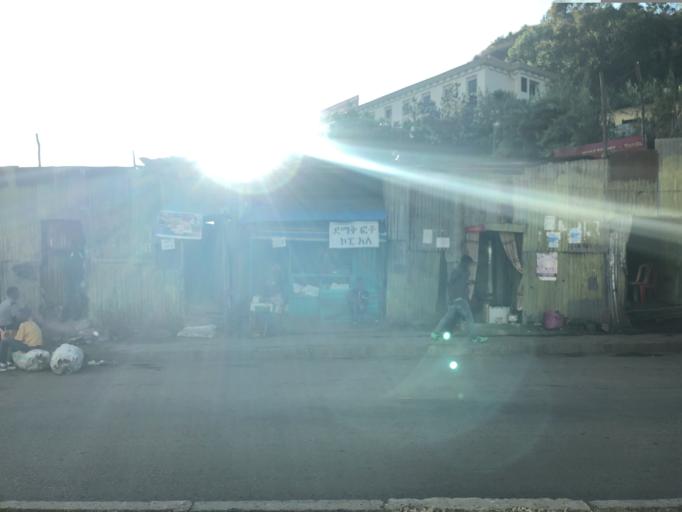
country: ET
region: Amhara
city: Gondar
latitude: 12.6187
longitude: 37.4706
